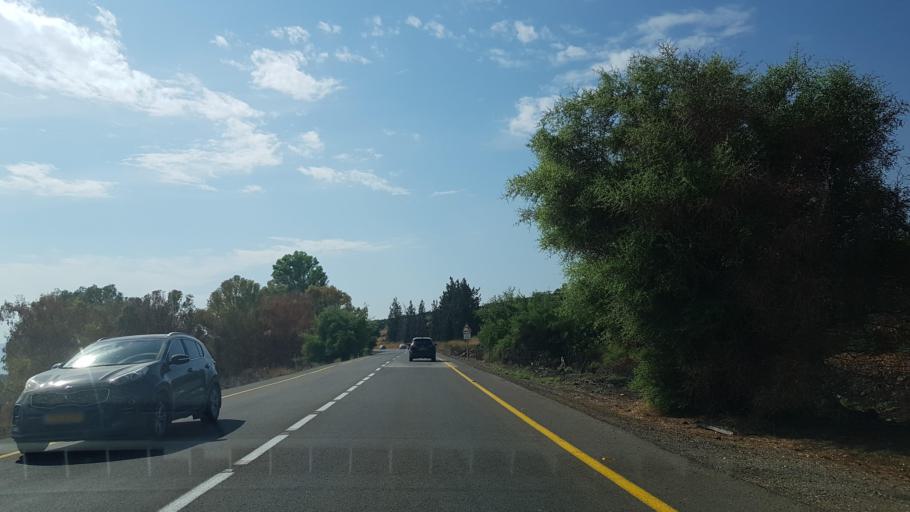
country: SY
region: Quneitra
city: Al Butayhah
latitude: 32.8971
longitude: 35.6067
